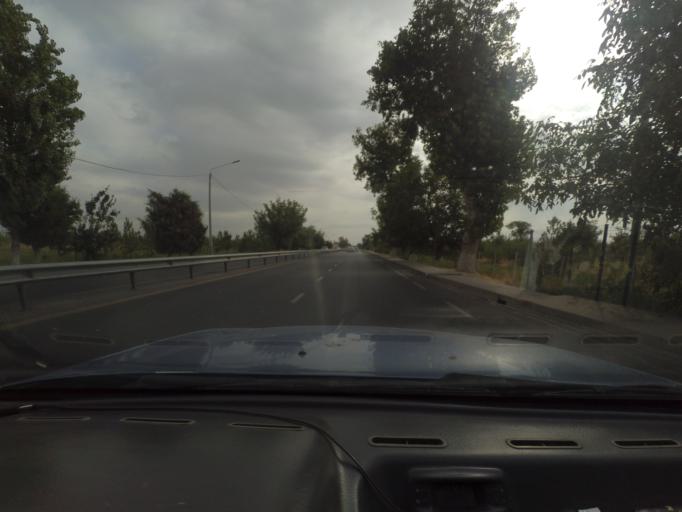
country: UZ
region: Toshkent
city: Qibray
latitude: 41.3955
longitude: 69.4786
